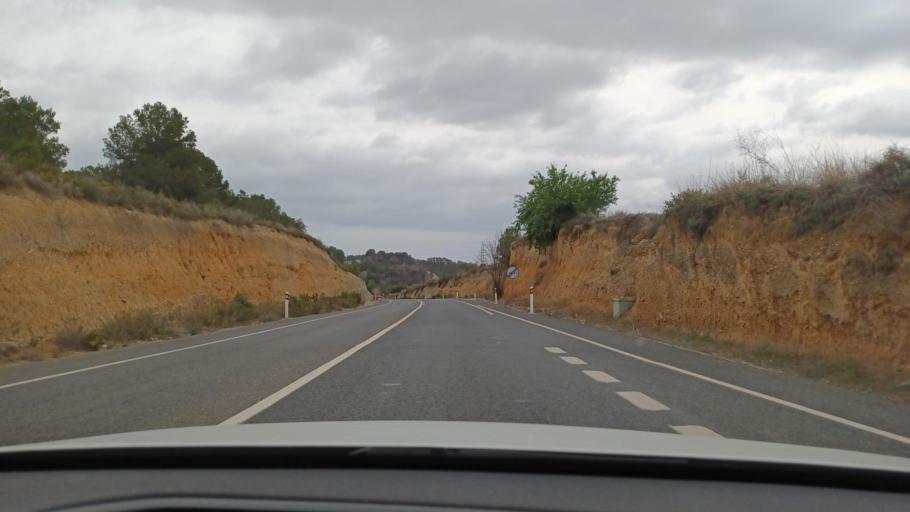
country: ES
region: Catalonia
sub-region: Provincia de Tarragona
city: la Pobla de Mafumet
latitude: 41.1721
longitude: 1.2396
